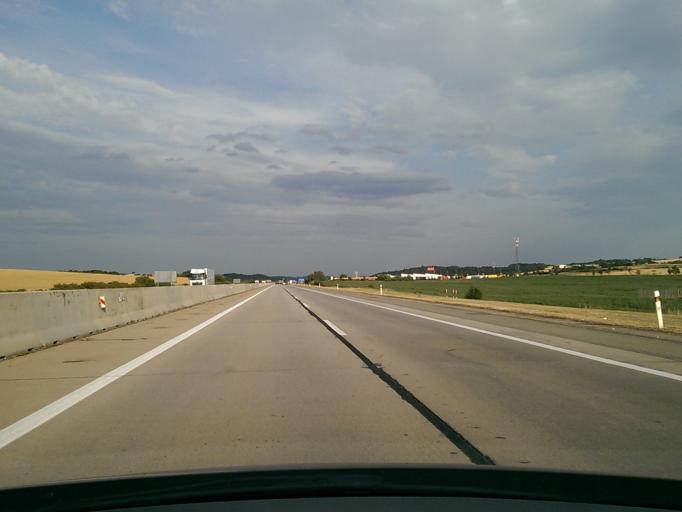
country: CZ
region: Vysocina
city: Merin
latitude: 49.3814
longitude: 15.9374
